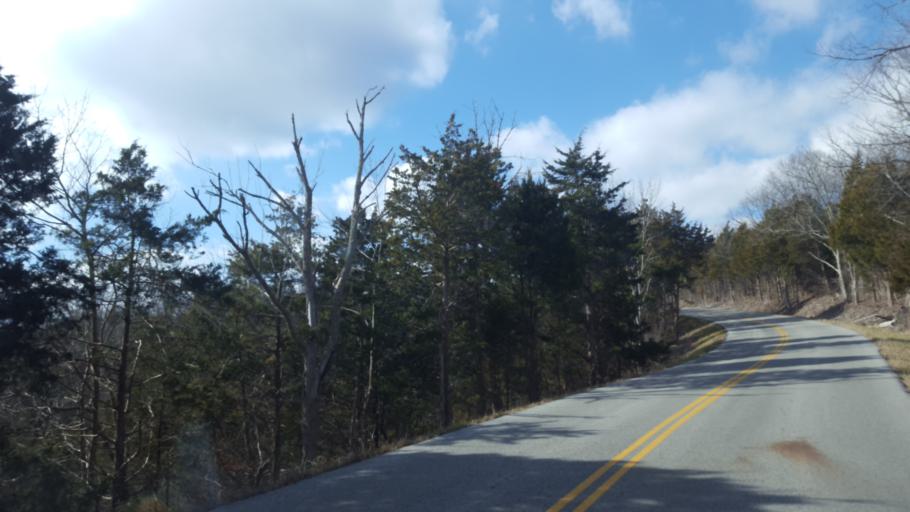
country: US
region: Kentucky
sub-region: Franklin County
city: Frankfort
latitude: 38.3752
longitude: -84.9386
